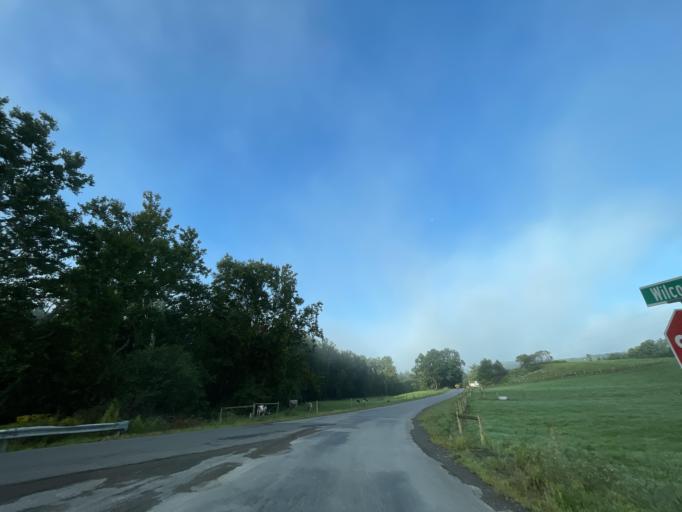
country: US
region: New York
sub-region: Chenango County
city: Oxford
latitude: 42.3901
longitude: -75.6201
